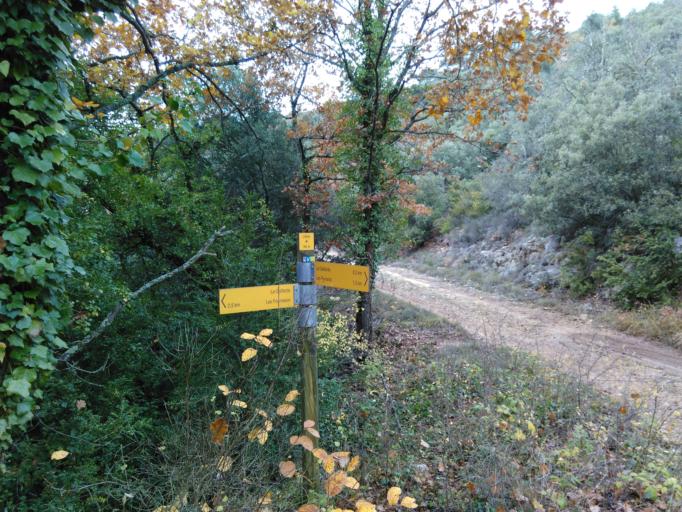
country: FR
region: Provence-Alpes-Cote d'Azur
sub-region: Departement du Vaucluse
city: Villes-sur-Auzon
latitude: 44.0482
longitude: 5.2754
